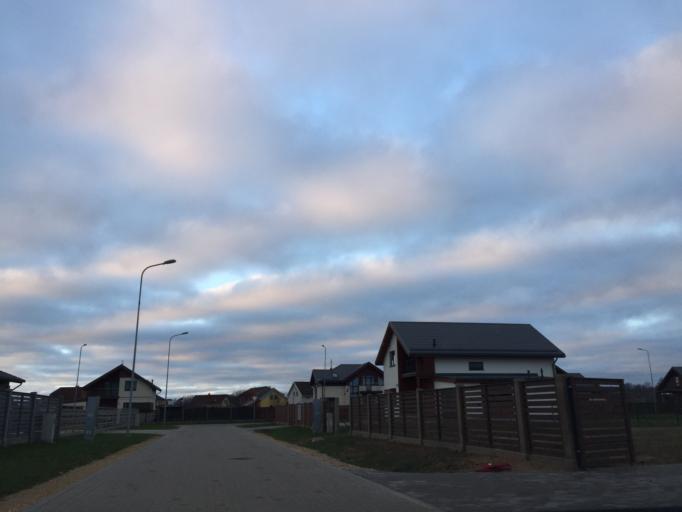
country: LV
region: Adazi
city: Adazi
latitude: 57.0675
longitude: 24.3466
